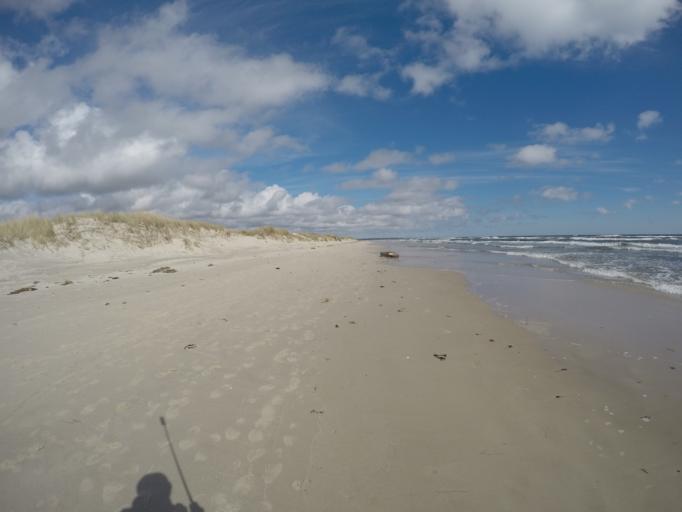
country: SE
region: Skane
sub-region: Simrishamns Kommun
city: Simrishamn
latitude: 55.3967
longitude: 14.2121
